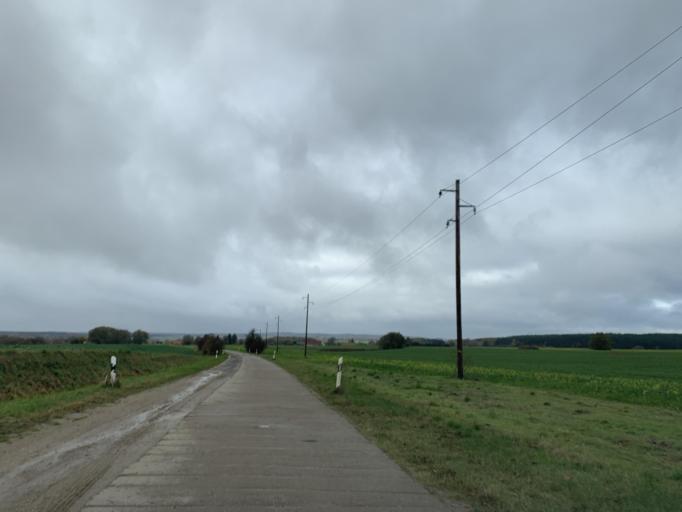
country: DE
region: Mecklenburg-Vorpommern
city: Blankensee
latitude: 53.3794
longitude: 13.2752
